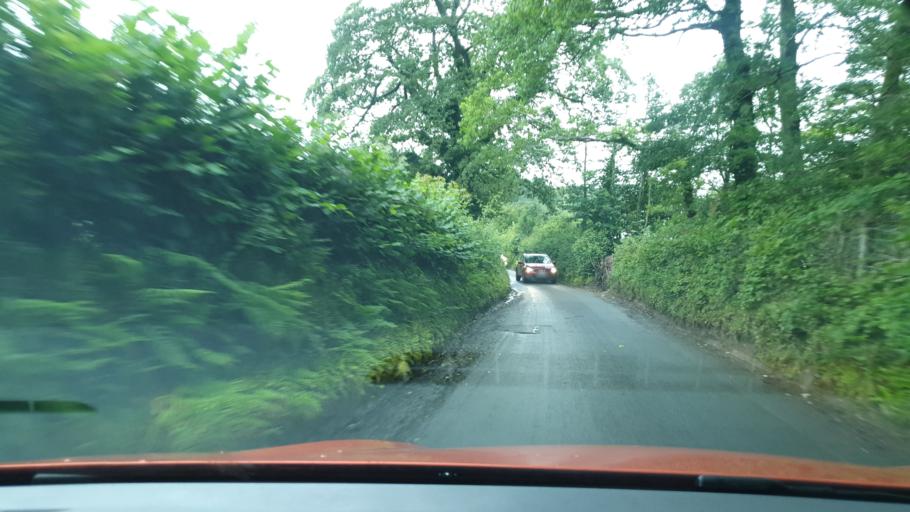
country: GB
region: England
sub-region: Cumbria
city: Seascale
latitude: 54.4039
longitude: -3.3704
